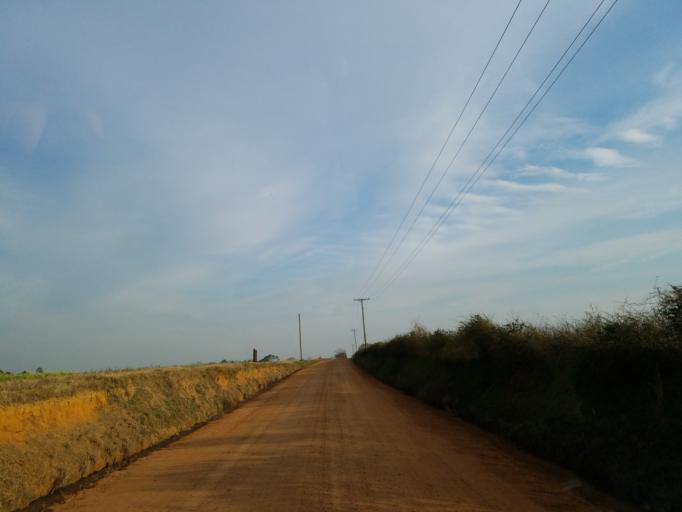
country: US
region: Georgia
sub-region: Tift County
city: Omega
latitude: 31.3771
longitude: -83.6209
